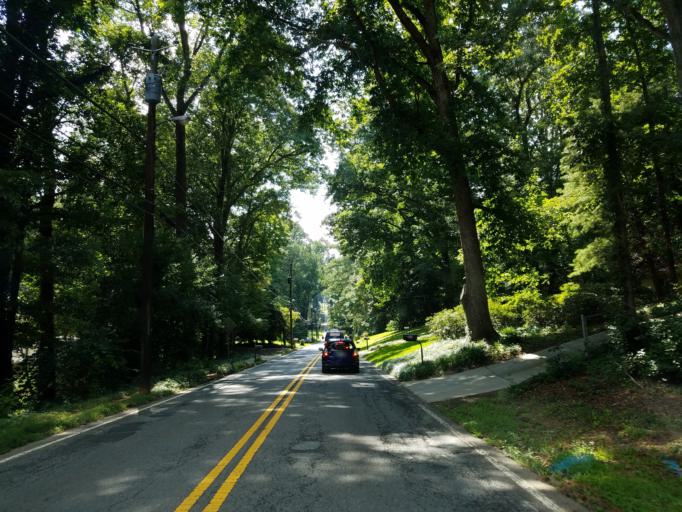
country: US
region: Georgia
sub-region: Fulton County
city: Sandy Springs
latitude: 33.9191
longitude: -84.3694
